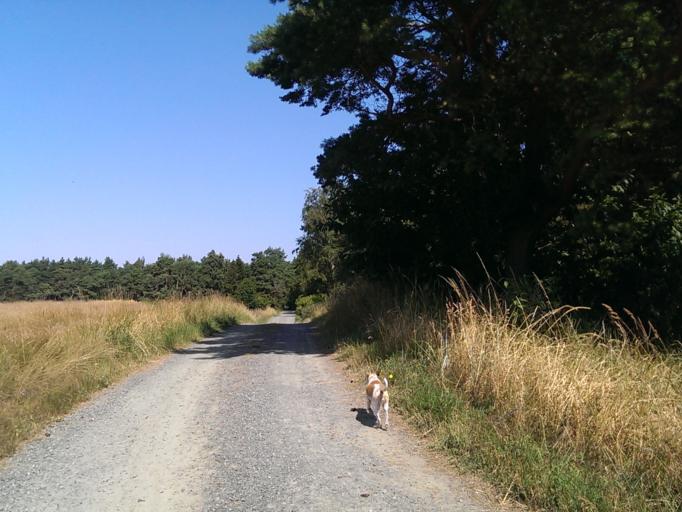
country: SE
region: Skane
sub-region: Simrishamns Kommun
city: Simrishamn
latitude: 55.4280
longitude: 14.2224
